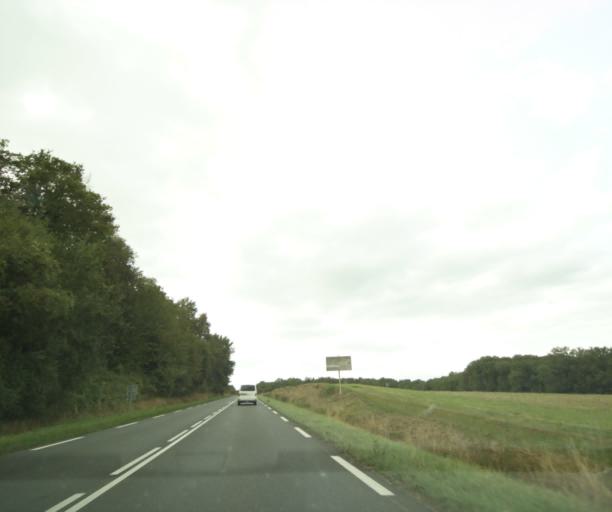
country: FR
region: Centre
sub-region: Departement d'Indre-et-Loire
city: Chambourg-sur-Indre
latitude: 47.1730
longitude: 0.9756
